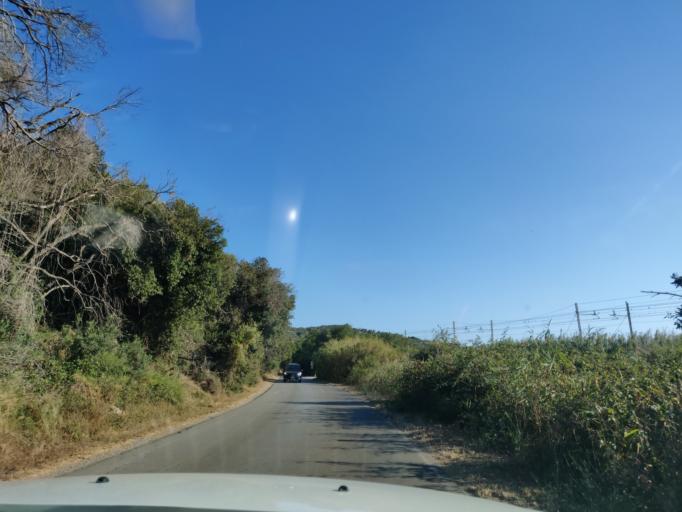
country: IT
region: Tuscany
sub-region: Provincia di Grosseto
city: Orbetello Scalo
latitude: 42.4228
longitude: 11.2819
